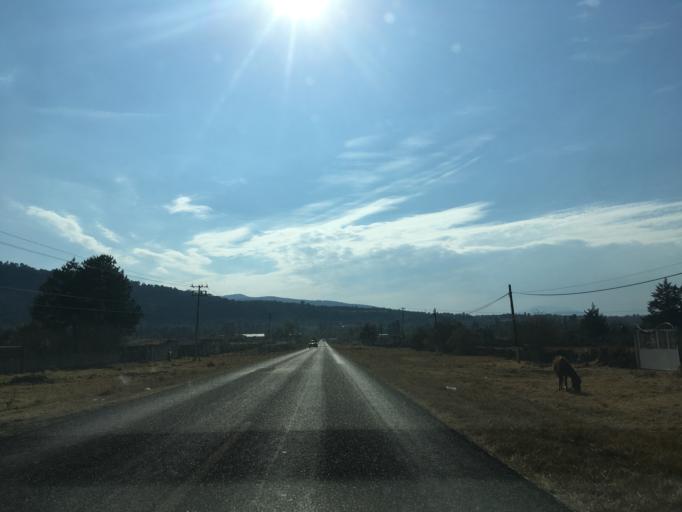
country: MX
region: Michoacan
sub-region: Patzcuaro
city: Santa Ana Chapitiro
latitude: 19.5328
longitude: -101.6421
